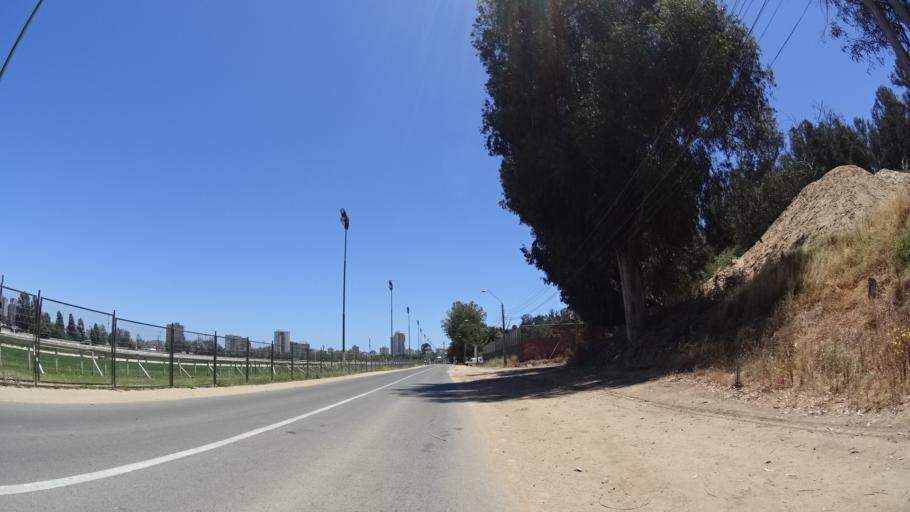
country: CL
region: Valparaiso
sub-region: Provincia de Valparaiso
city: Vina del Mar
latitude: -33.0240
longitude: -71.5337
